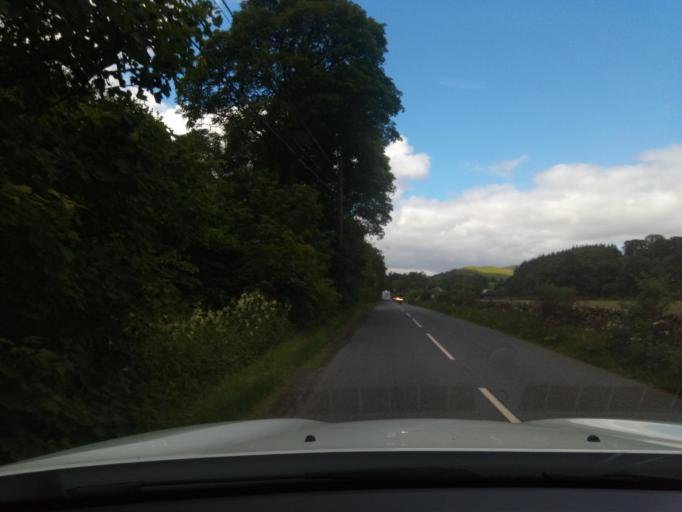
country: GB
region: Scotland
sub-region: The Scottish Borders
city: Selkirk
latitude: 55.5577
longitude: -2.9503
